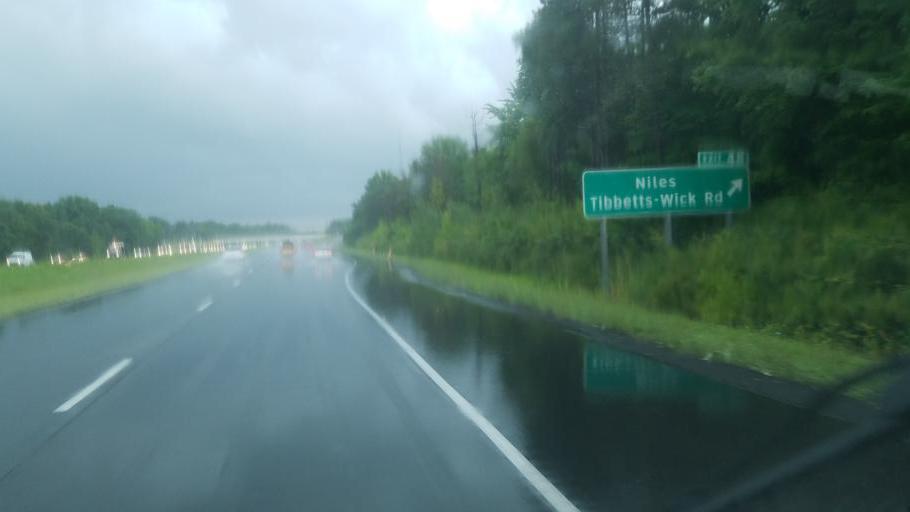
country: US
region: Ohio
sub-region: Trumbull County
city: McKinley Heights
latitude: 41.1893
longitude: -80.6954
